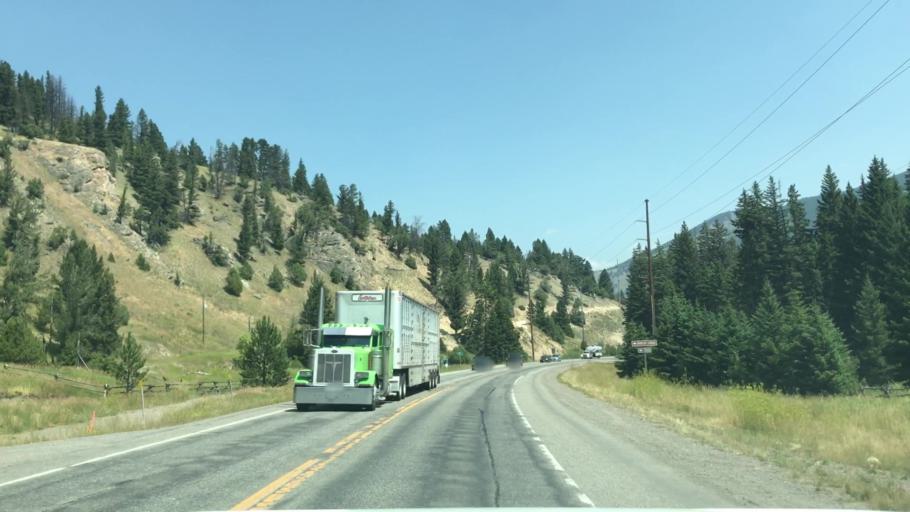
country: US
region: Montana
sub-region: Gallatin County
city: Big Sky
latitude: 45.2684
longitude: -111.2506
